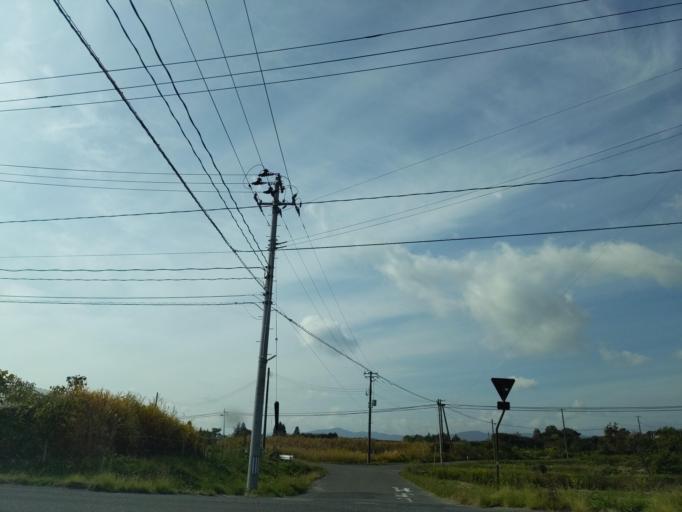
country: JP
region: Fukushima
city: Koriyama
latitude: 37.4345
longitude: 140.3123
